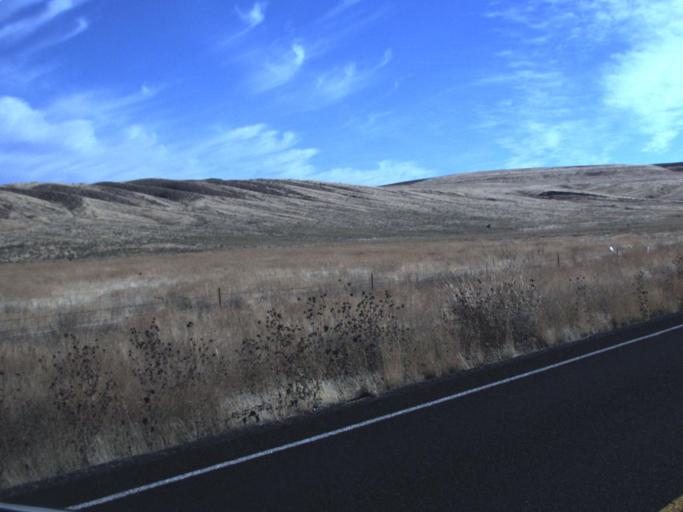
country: US
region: Washington
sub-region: Franklin County
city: Connell
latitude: 46.6496
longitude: -118.6069
